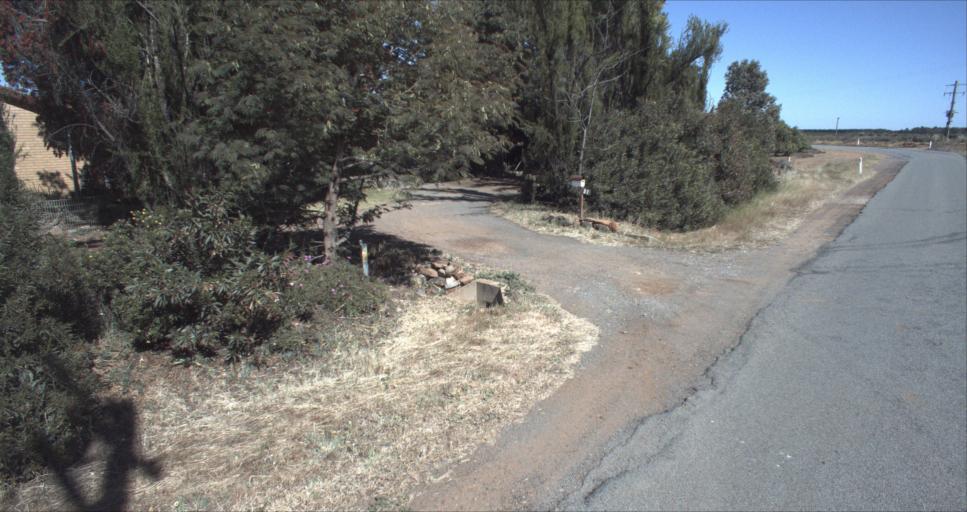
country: AU
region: New South Wales
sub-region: Leeton
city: Leeton
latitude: -34.5402
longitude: 146.3405
